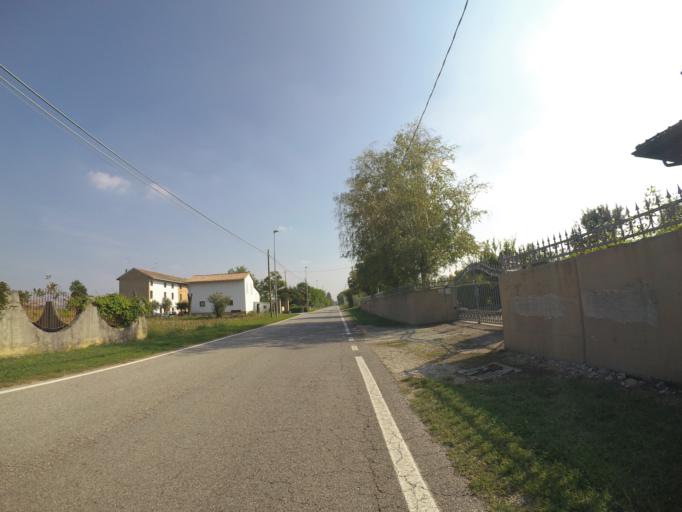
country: IT
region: Friuli Venezia Giulia
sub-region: Provincia di Udine
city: Basiliano
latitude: 45.9920
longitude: 13.0297
